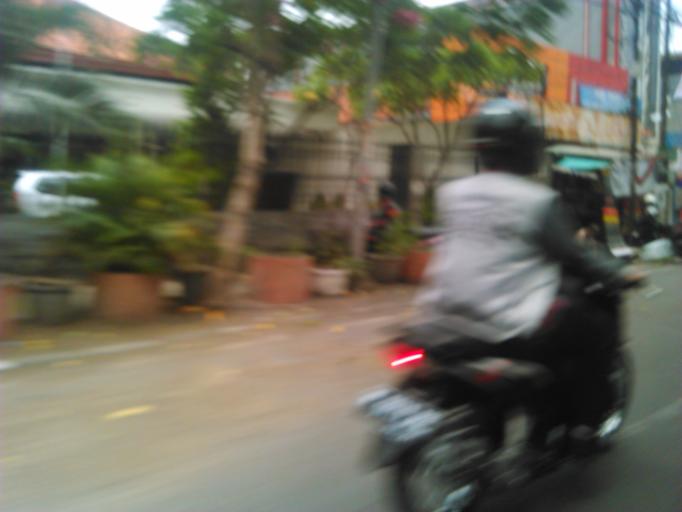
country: ID
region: East Java
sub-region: Kota Surabaya
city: Surabaya
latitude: -7.2619
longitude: 112.7268
